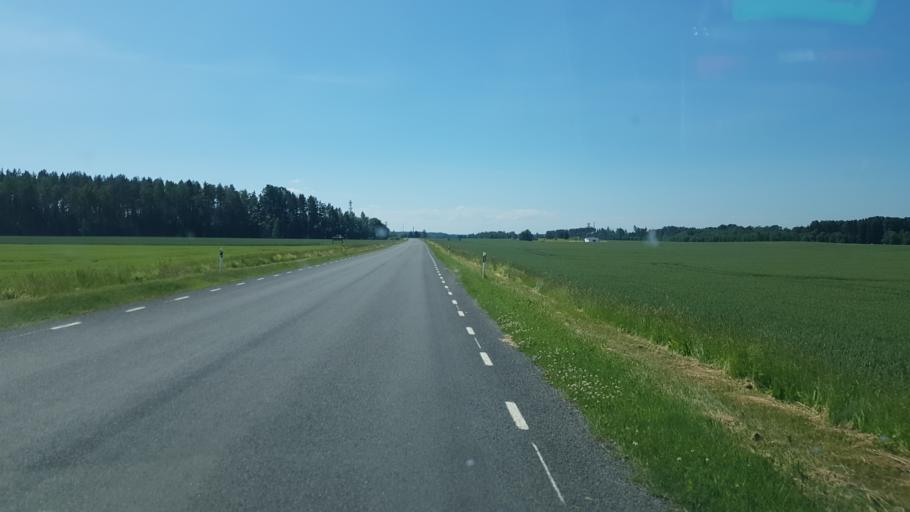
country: EE
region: Tartu
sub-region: UElenurme vald
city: Ulenurme
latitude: 58.3145
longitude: 26.8829
